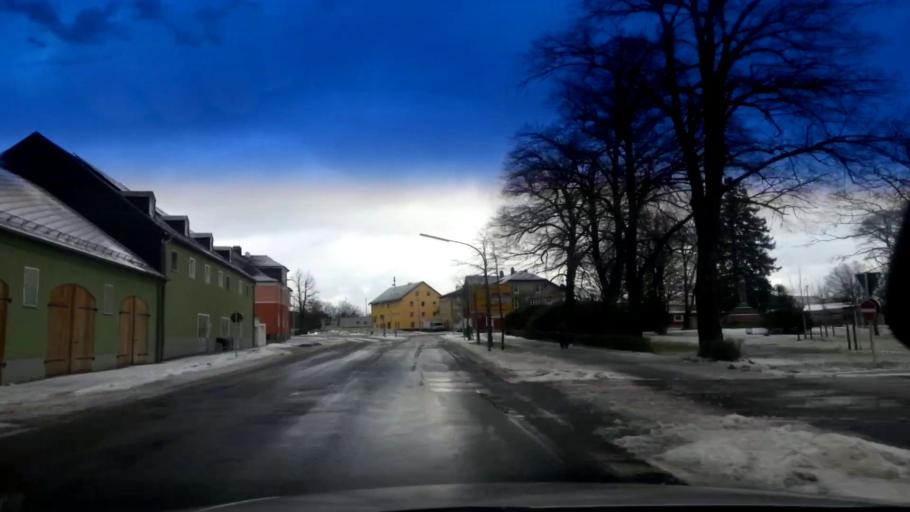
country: DE
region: Bavaria
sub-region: Upper Franconia
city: Weissenstadt
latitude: 50.1045
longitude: 11.8877
